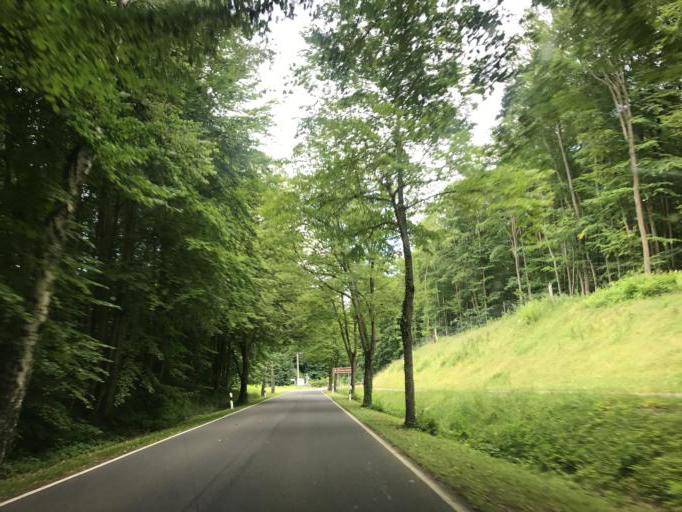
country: DE
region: Mecklenburg-Vorpommern
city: Wesenberg
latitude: 53.2164
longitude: 12.9373
